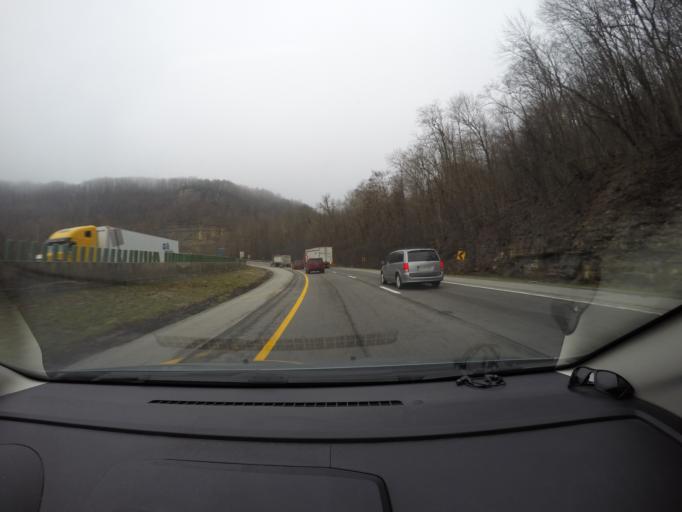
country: US
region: Tennessee
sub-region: Marion County
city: Monteagle
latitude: 35.2402
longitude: -85.8764
